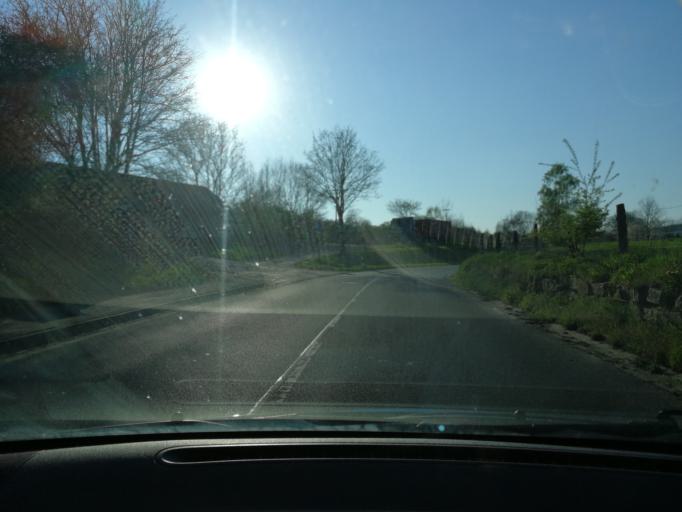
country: DE
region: Lower Saxony
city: Uslar
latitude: 51.6141
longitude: 9.6648
